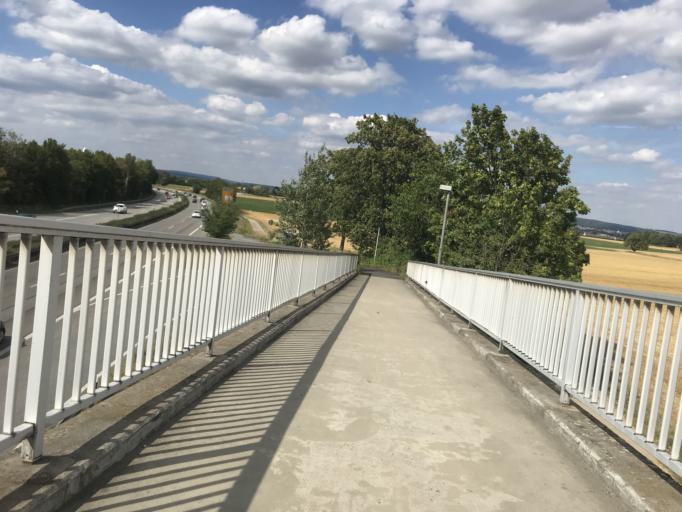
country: DE
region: Rheinland-Pfalz
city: Mainz
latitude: 50.0382
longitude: 8.2980
